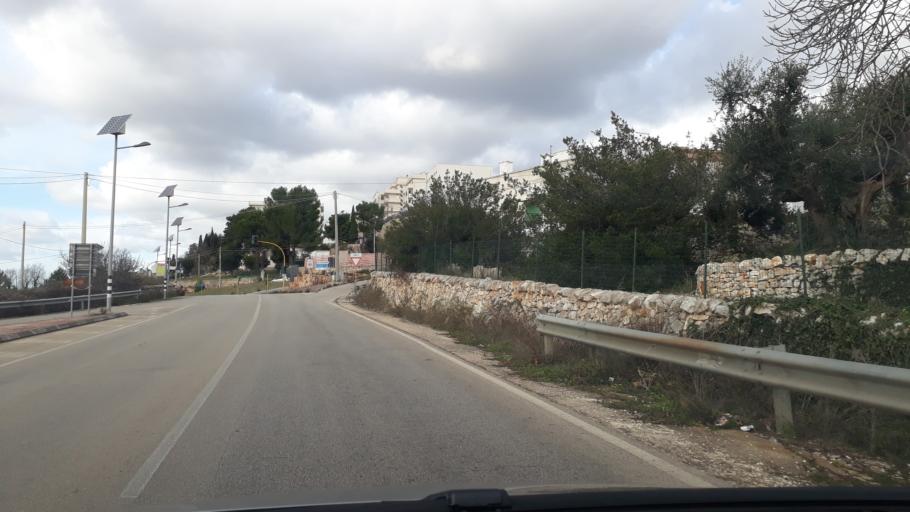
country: IT
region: Apulia
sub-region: Provincia di Brindisi
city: Cisternino
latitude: 40.7380
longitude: 17.4301
